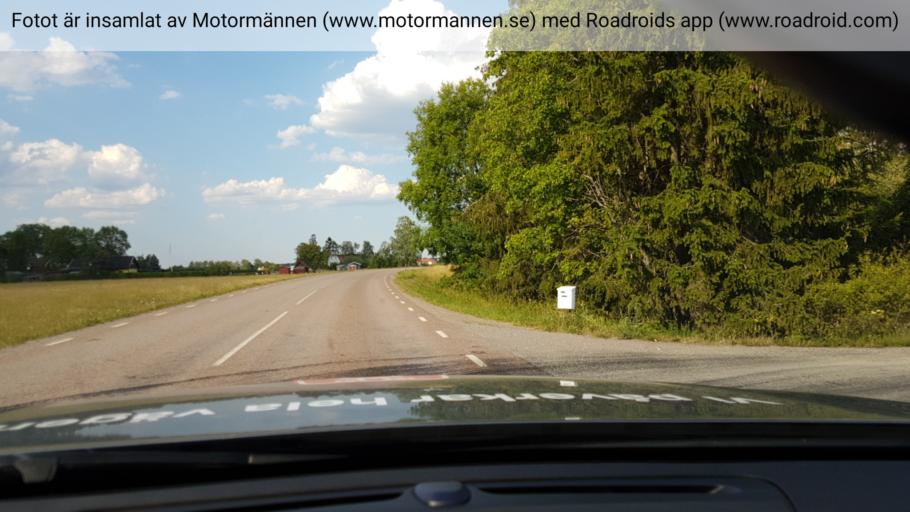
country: SE
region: Vaestmanland
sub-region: Vasteras
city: Tillberga
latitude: 59.6931
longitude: 16.6217
